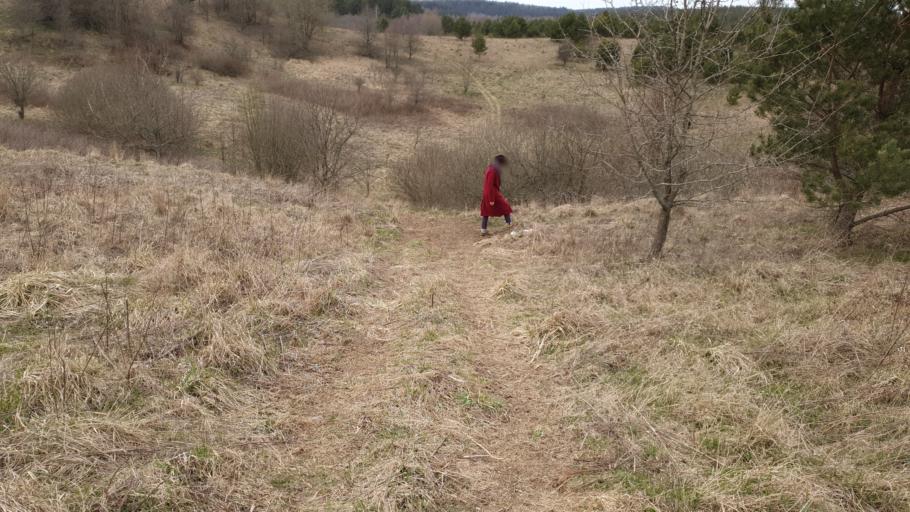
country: LT
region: Vilnius County
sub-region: Vilniaus Rajonas
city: Vievis
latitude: 54.6419
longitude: 24.7324
